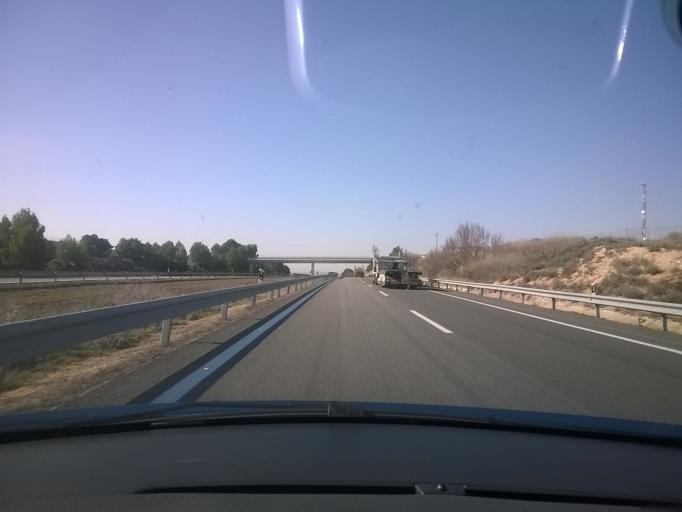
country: ES
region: Aragon
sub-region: Provincia de Huesca
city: Penalba
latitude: 41.5116
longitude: -0.0173
